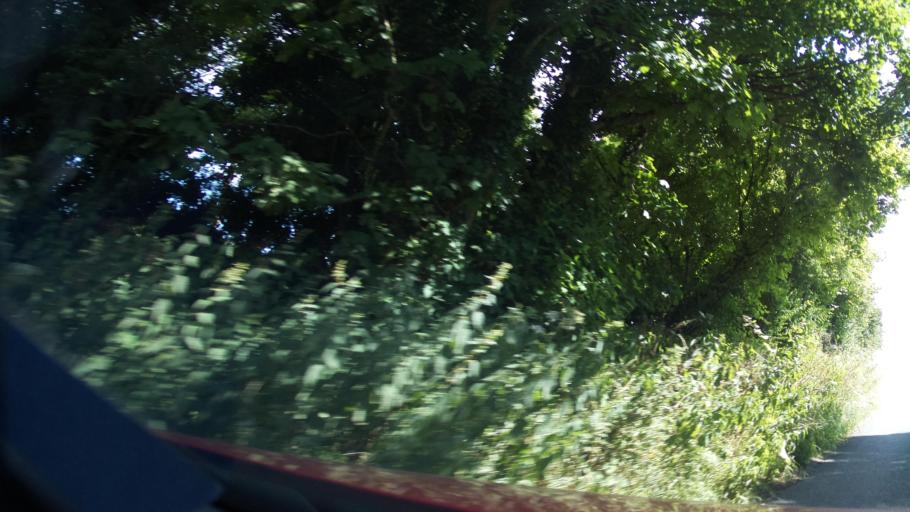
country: GB
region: England
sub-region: Borough of Swindon
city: Bishopstone
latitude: 51.5617
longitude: -1.6150
